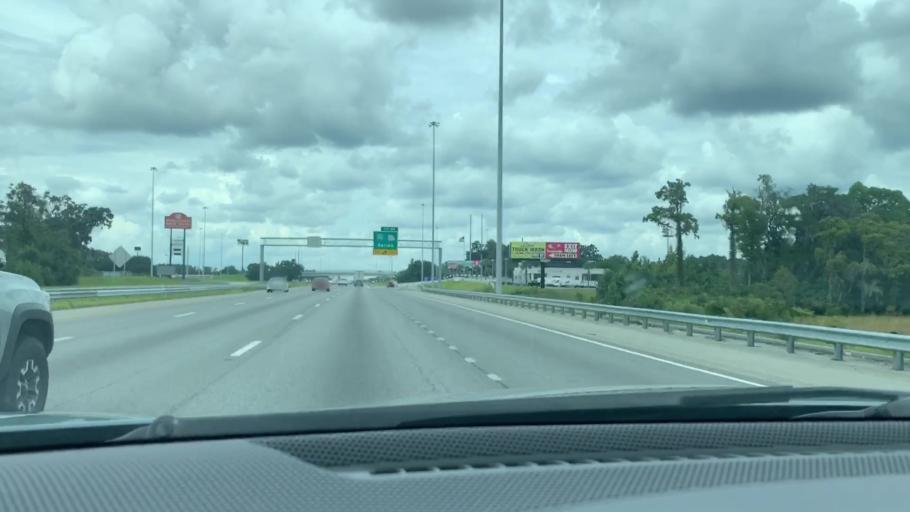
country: US
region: Georgia
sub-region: McIntosh County
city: Darien
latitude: 31.3904
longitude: -81.4500
